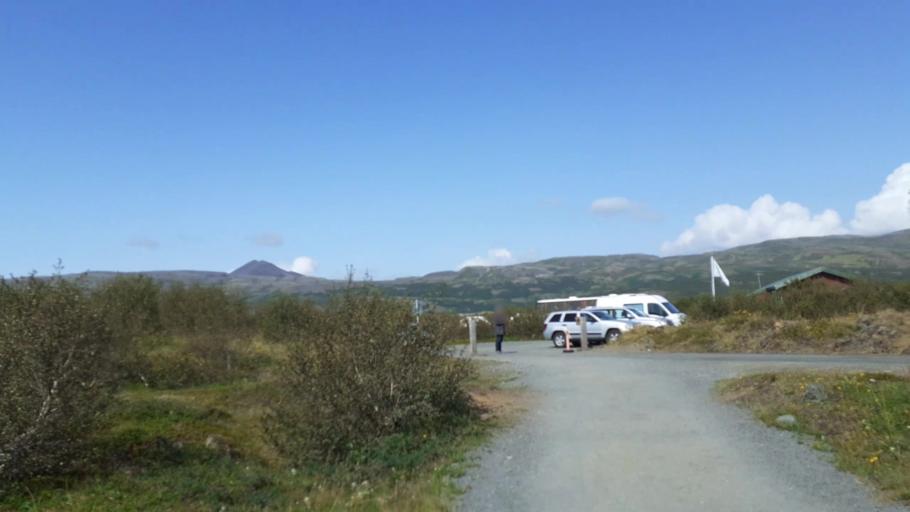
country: IS
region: West
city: Borgarnes
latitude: 64.7555
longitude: -21.5472
